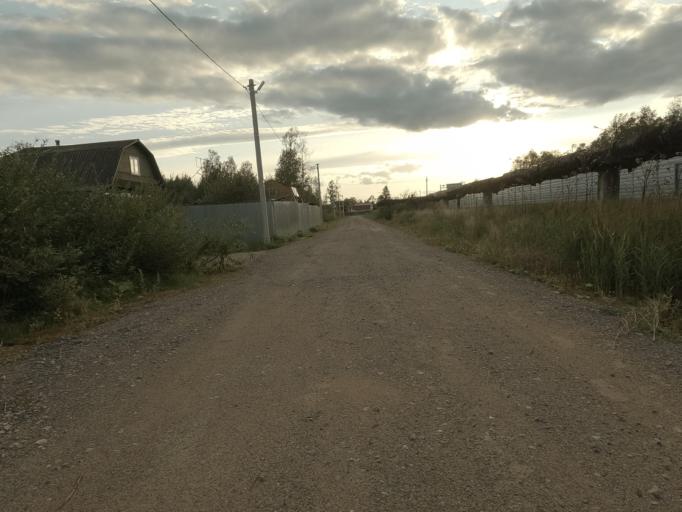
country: RU
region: Leningrad
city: Mga
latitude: 59.7570
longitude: 31.0844
